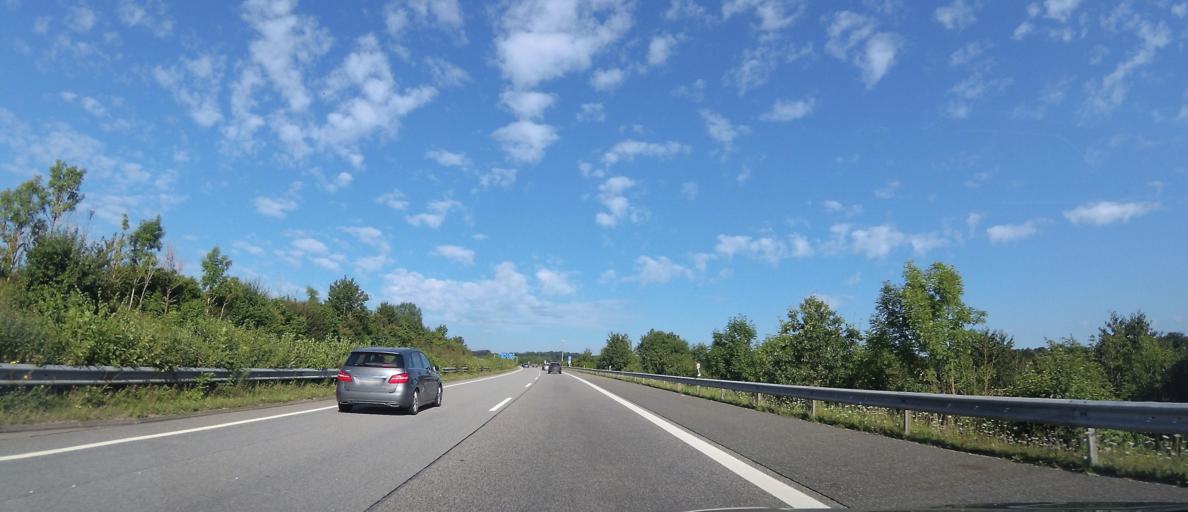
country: DE
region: Rheinland-Pfalz
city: Malbergweich
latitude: 50.0355
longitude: 6.5405
